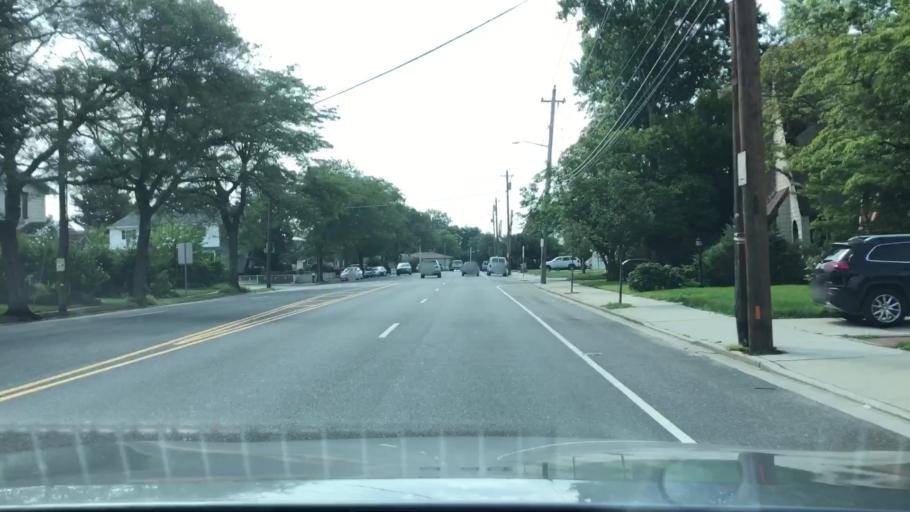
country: US
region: New York
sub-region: Nassau County
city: South Hempstead
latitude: 40.6747
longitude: -73.6123
